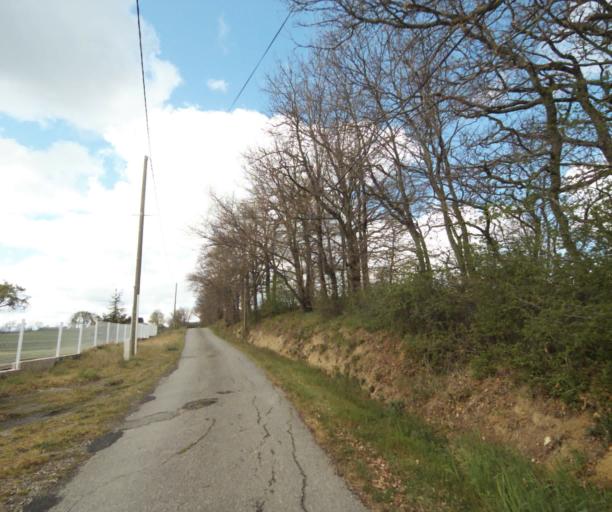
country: FR
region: Midi-Pyrenees
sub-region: Departement de l'Ariege
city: Saverdun
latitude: 43.1963
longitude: 1.5745
